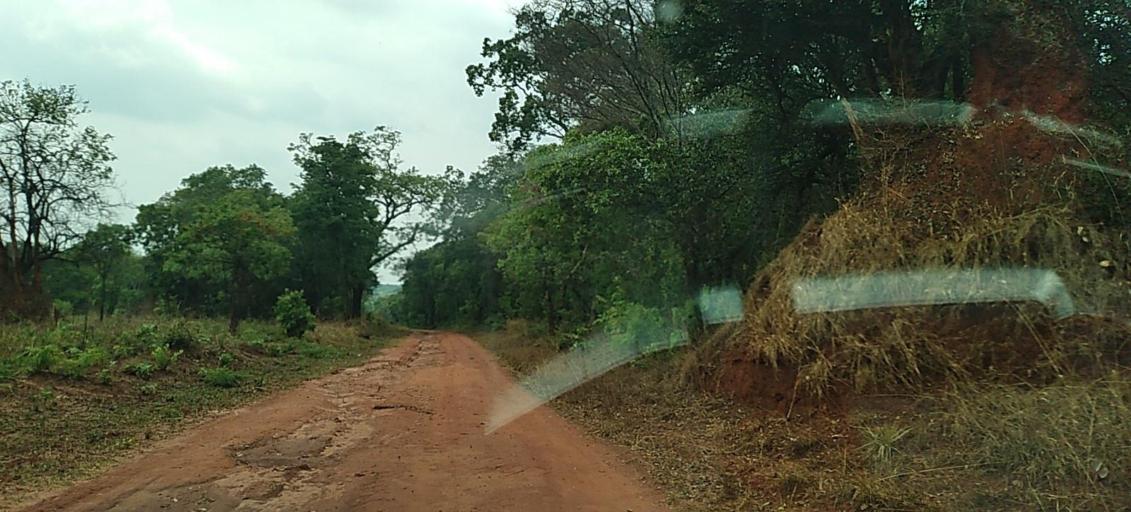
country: ZM
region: North-Western
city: Mwinilunga
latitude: -11.5421
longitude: 24.7803
